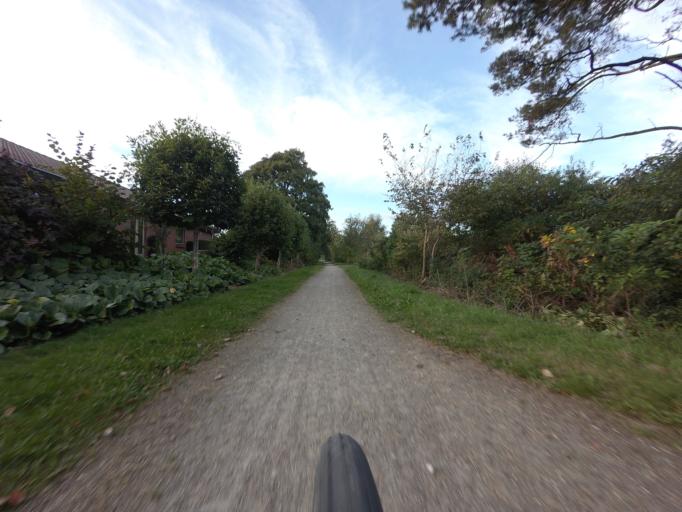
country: DK
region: Central Jutland
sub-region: Ikast-Brande Kommune
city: Brande
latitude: 55.9361
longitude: 9.1427
